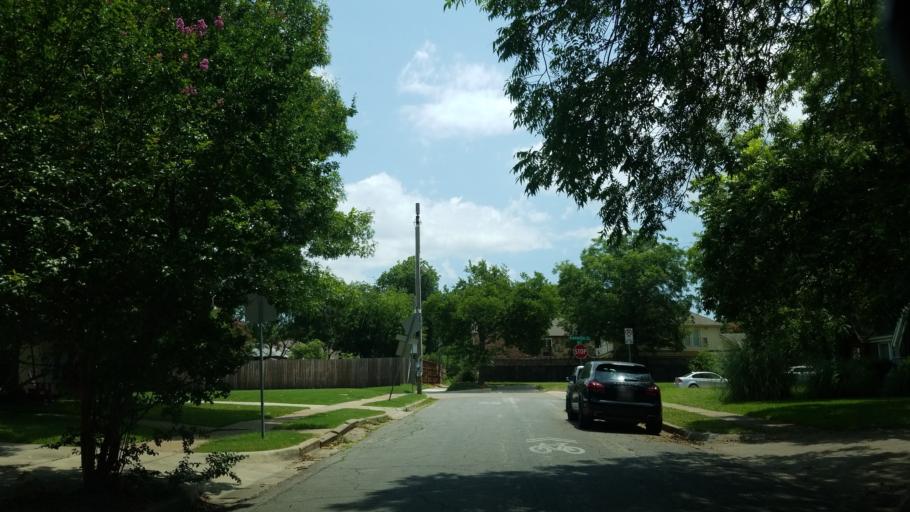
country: US
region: Texas
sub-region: Dallas County
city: Highland Park
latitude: 32.8265
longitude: -96.7707
